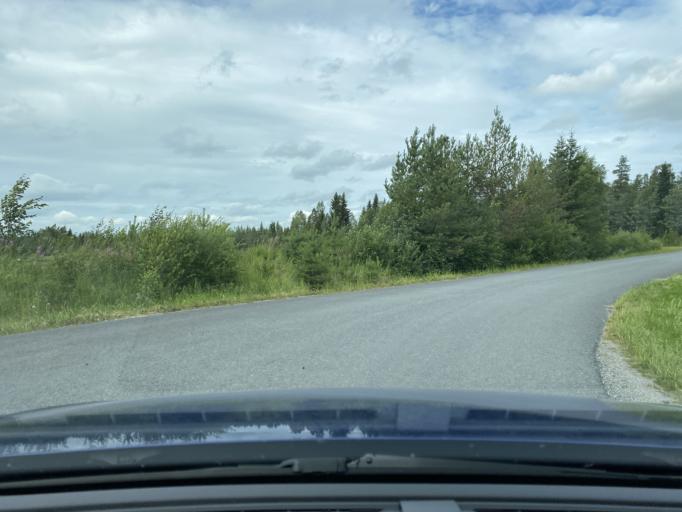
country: FI
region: Southern Ostrobothnia
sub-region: Seinaejoki
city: Jurva
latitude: 62.6256
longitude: 22.0278
